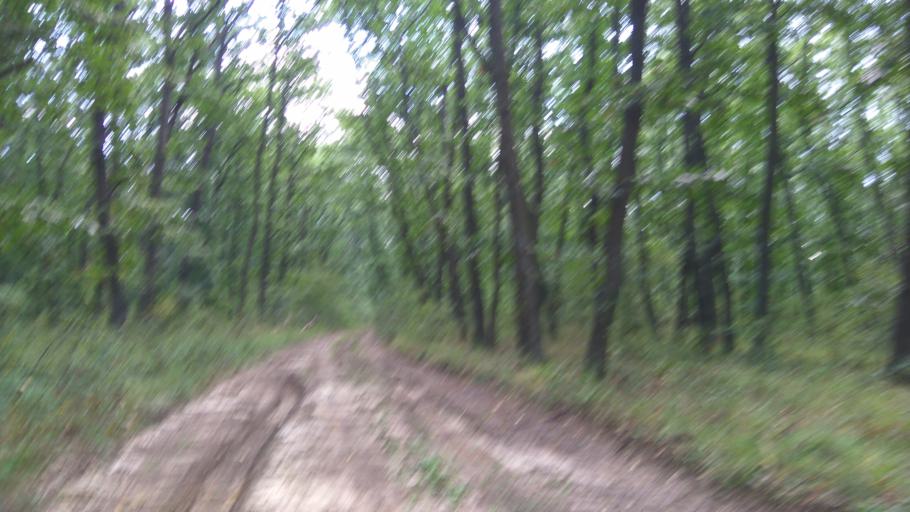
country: SK
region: Nitriansky
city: Sahy
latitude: 48.0157
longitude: 18.9298
